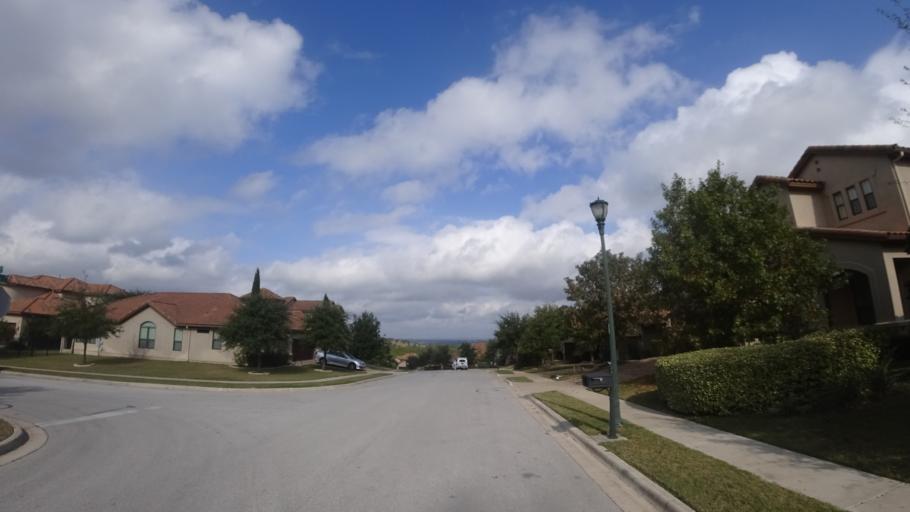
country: US
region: Texas
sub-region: Travis County
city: Bee Cave
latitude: 30.3119
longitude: -97.9030
